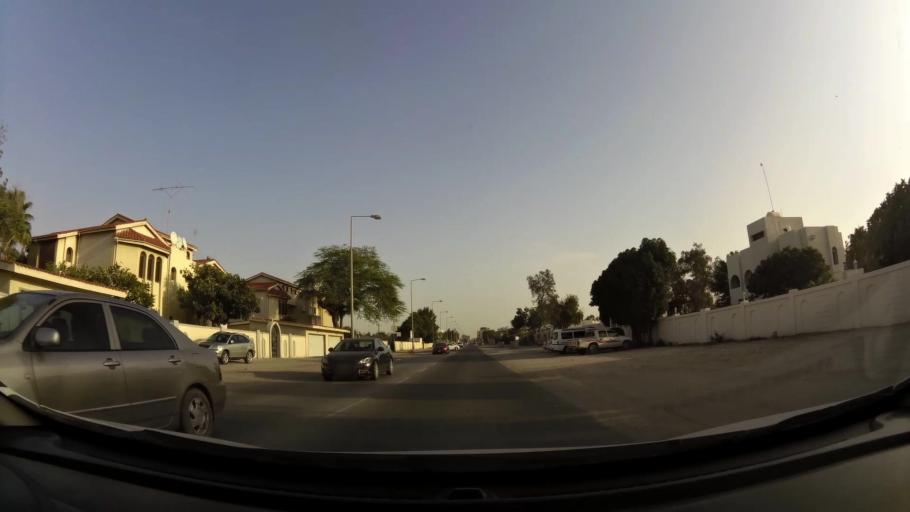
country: BH
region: Manama
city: Jidd Hafs
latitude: 26.2009
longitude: 50.4847
